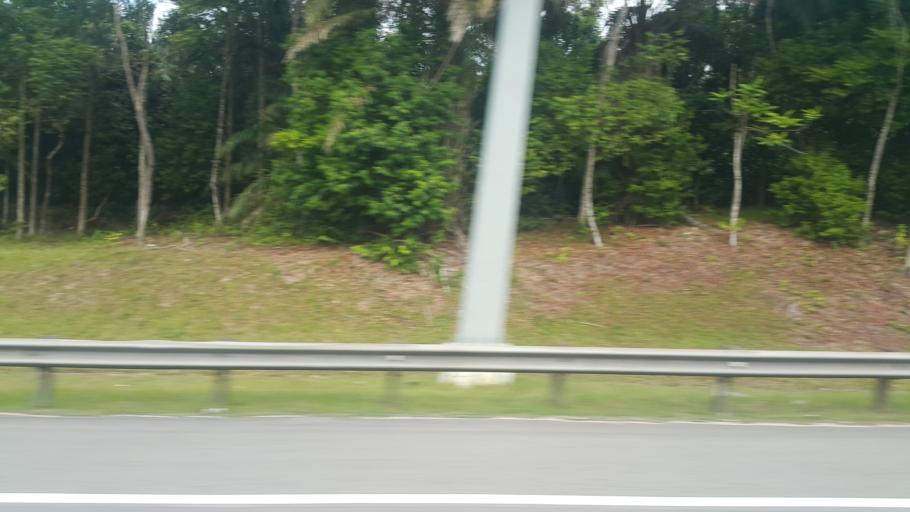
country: MY
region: Johor
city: Pekan Nenas
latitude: 1.4261
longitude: 103.6027
